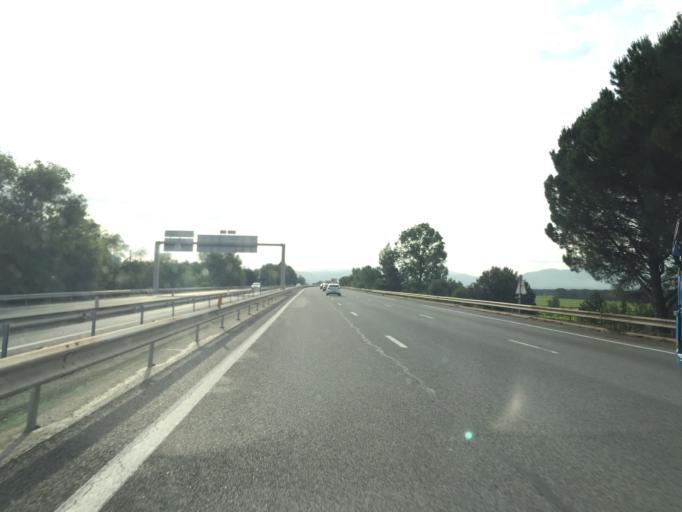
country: FR
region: Provence-Alpes-Cote d'Azur
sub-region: Departement du Var
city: Le Cannet-des-Maures
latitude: 43.4018
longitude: 6.3768
